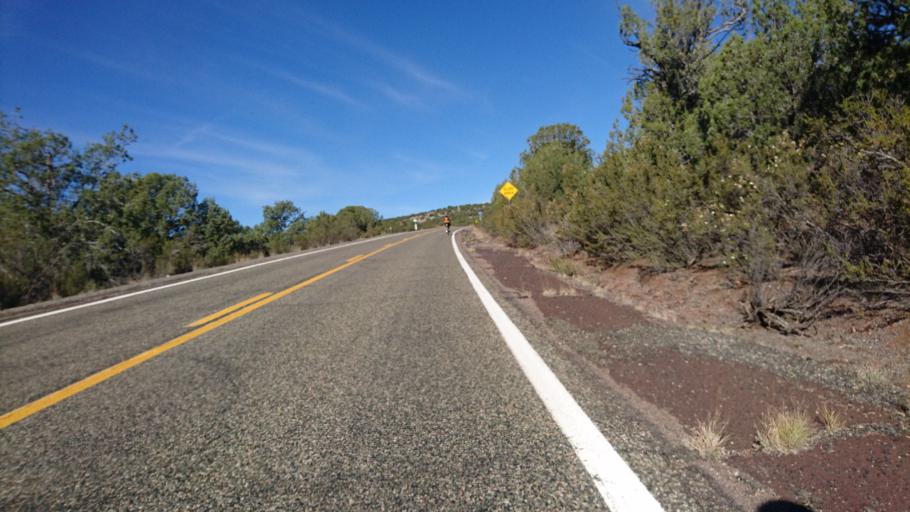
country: US
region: Arizona
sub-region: Yavapai County
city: Paulden
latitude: 35.2728
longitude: -112.6854
